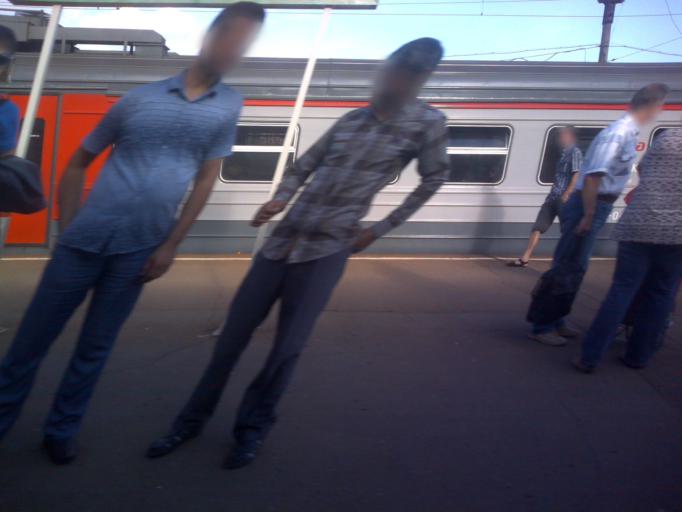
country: RU
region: Moscow
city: Nagornyy
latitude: 55.6557
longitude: 37.6225
